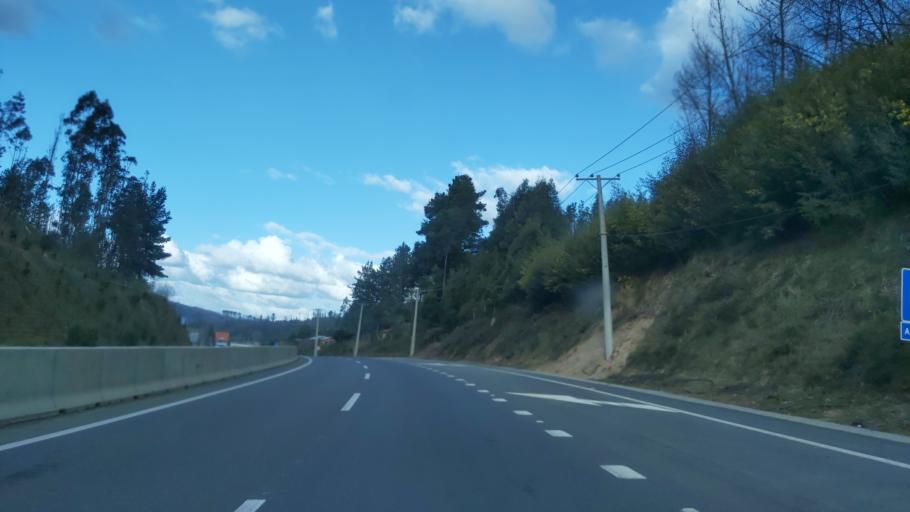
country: CL
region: Biobio
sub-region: Provincia de Concepcion
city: Chiguayante
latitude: -36.8549
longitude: -72.8951
